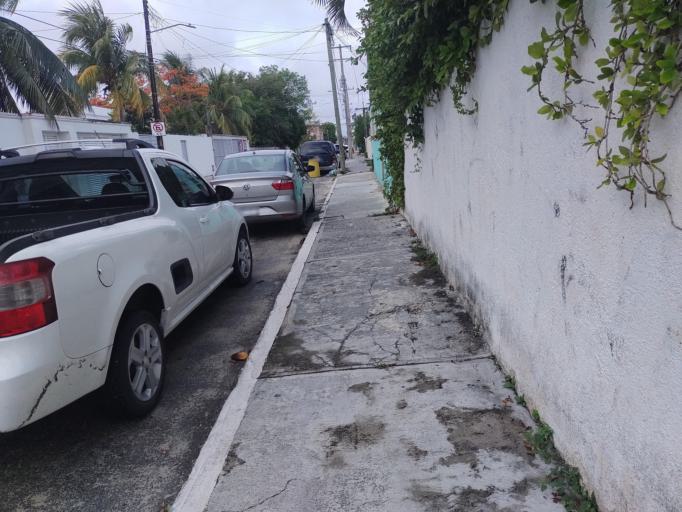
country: MX
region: Quintana Roo
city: San Miguel de Cozumel
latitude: 20.5092
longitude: -86.9444
